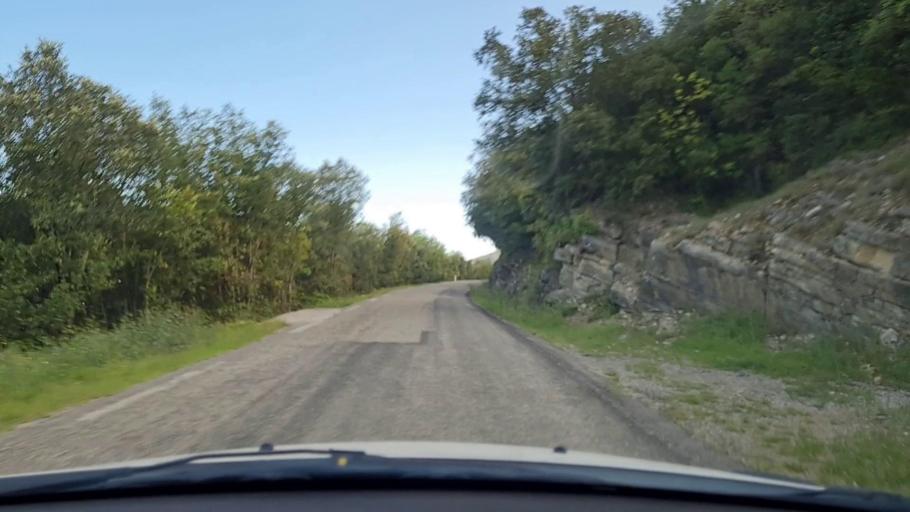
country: FR
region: Languedoc-Roussillon
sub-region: Departement du Gard
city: Les Salles-du-Gardon
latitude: 44.1684
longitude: 4.0244
